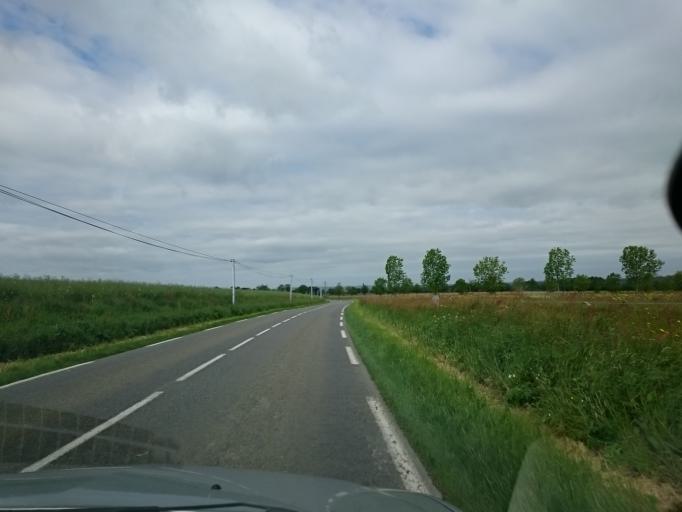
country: FR
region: Lower Normandy
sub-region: Departement de la Manche
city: Pontorson
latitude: 48.5538
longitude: -1.4359
